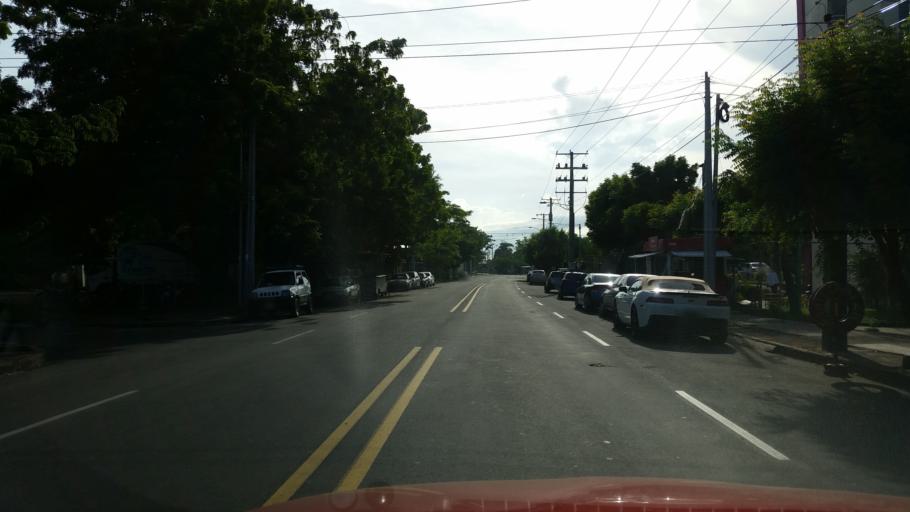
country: NI
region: Managua
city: Managua
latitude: 12.1566
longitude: -86.2745
